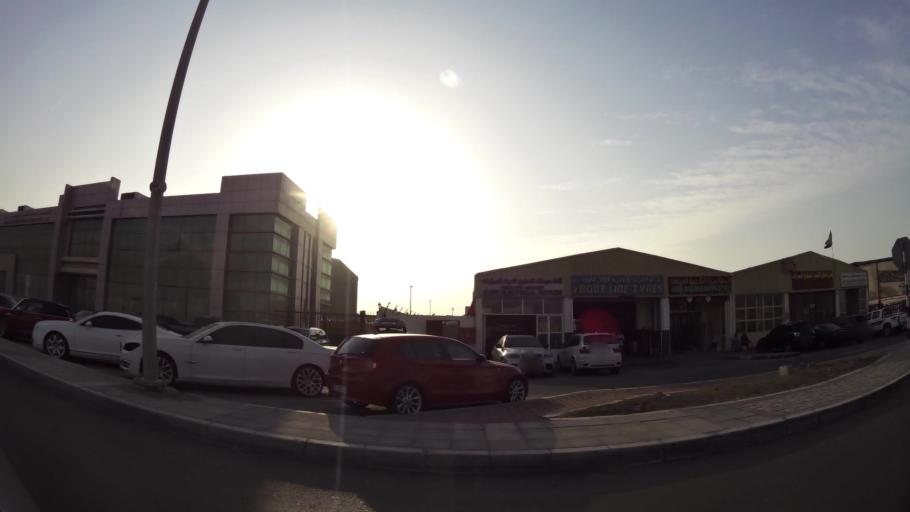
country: AE
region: Abu Dhabi
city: Abu Dhabi
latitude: 24.3636
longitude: 54.5113
